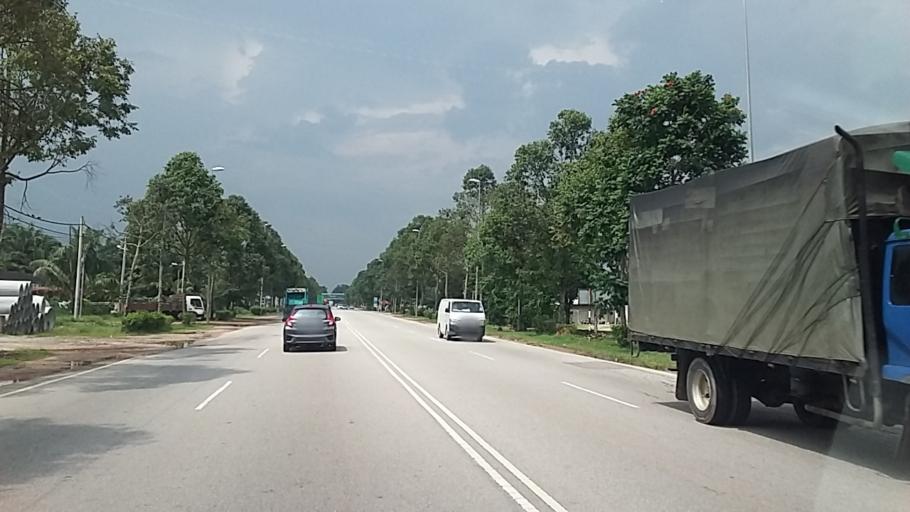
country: MY
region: Johor
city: Parit Raja
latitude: 1.8691
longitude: 103.1234
